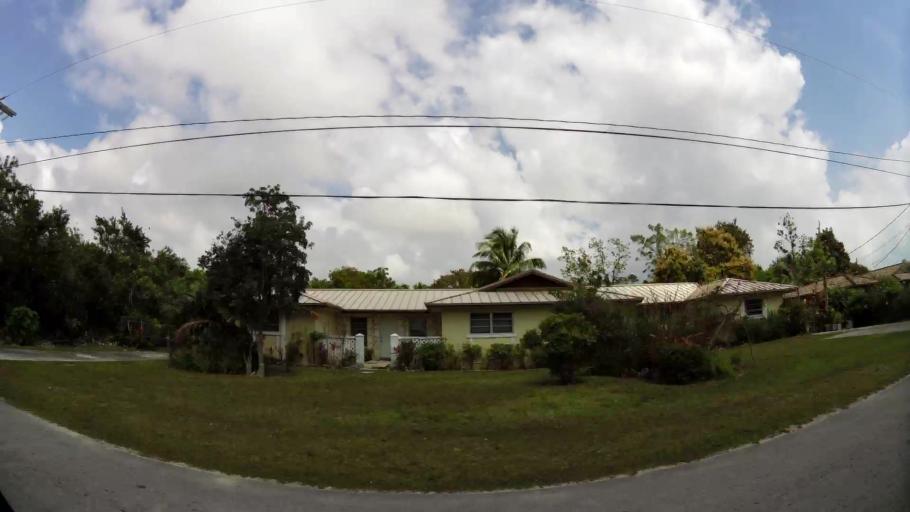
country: BS
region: Freeport
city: Lucaya
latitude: 26.5193
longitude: -78.6551
